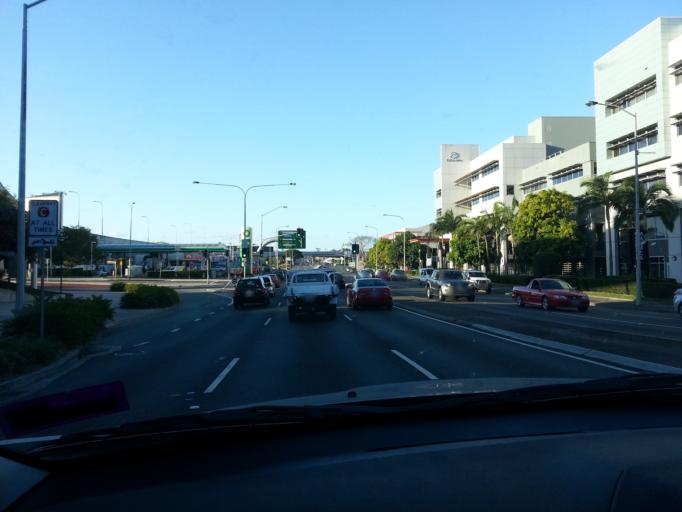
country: AU
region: Queensland
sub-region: Brisbane
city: Windsor
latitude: -27.4466
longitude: 153.0295
